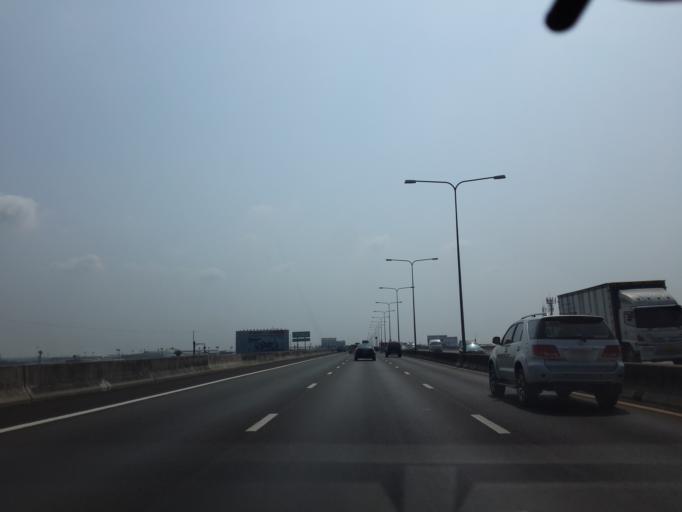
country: TH
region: Samut Prakan
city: Bang Bo District
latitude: 13.6013
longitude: 100.7871
